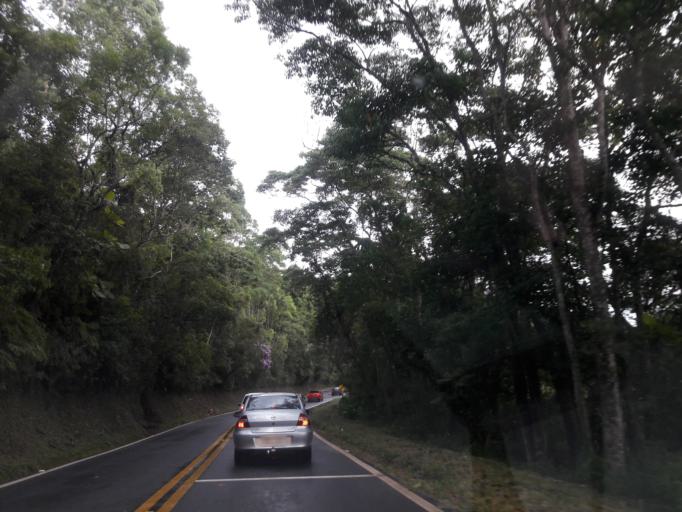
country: BR
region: Sao Paulo
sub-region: Aruja
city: Aruja
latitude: -23.3343
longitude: -46.4342
